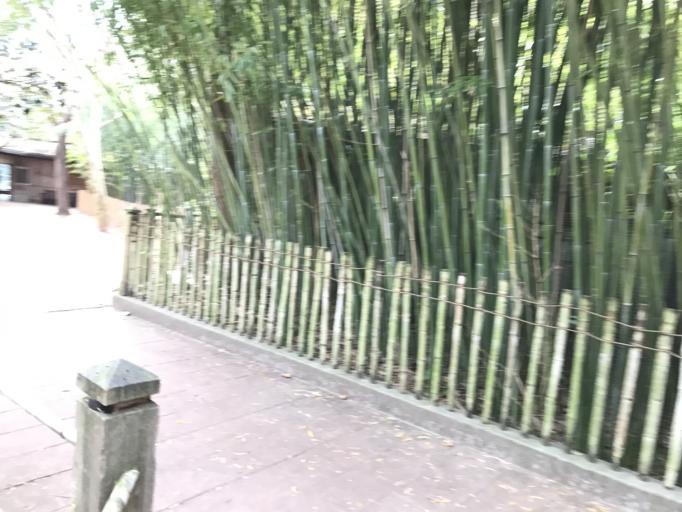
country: US
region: Kentucky
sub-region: Jefferson County
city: Audubon Park
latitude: 38.2047
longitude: -85.7079
